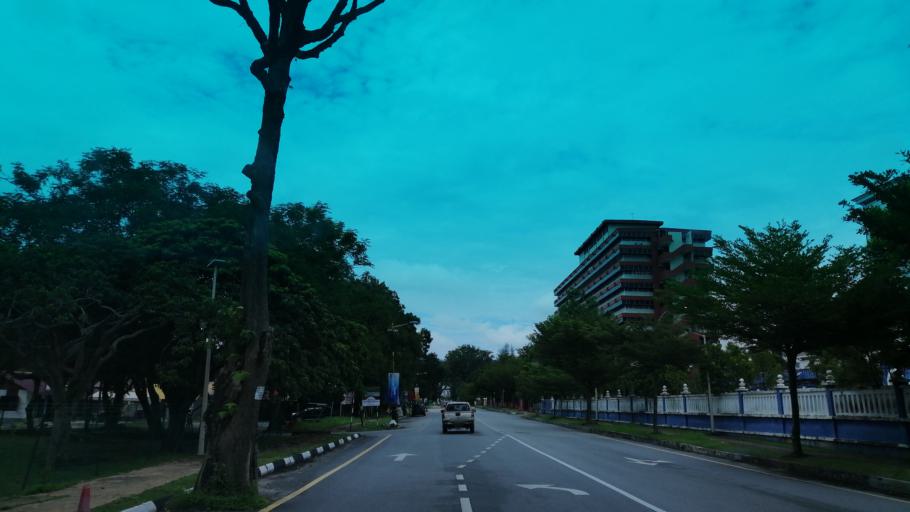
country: MY
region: Perak
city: Taiping
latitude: 4.8555
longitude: 100.7404
